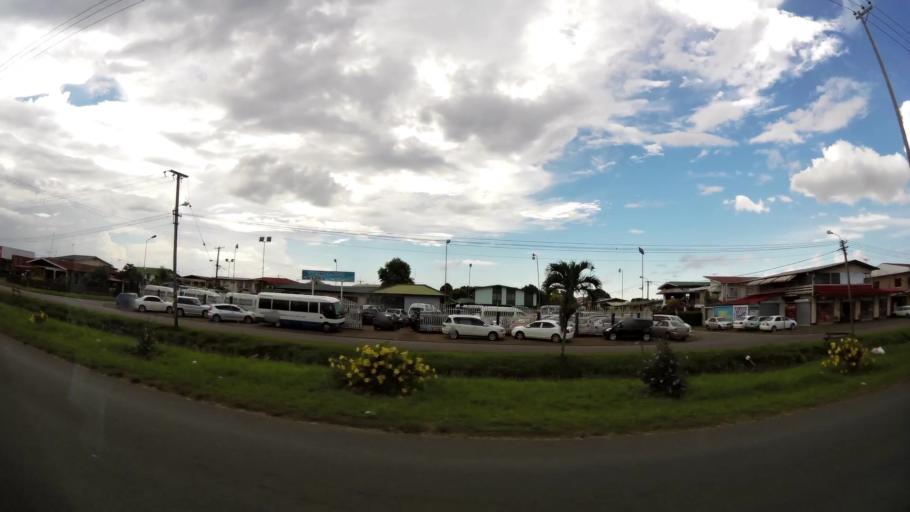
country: SR
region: Paramaribo
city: Paramaribo
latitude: 5.8431
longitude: -55.1381
